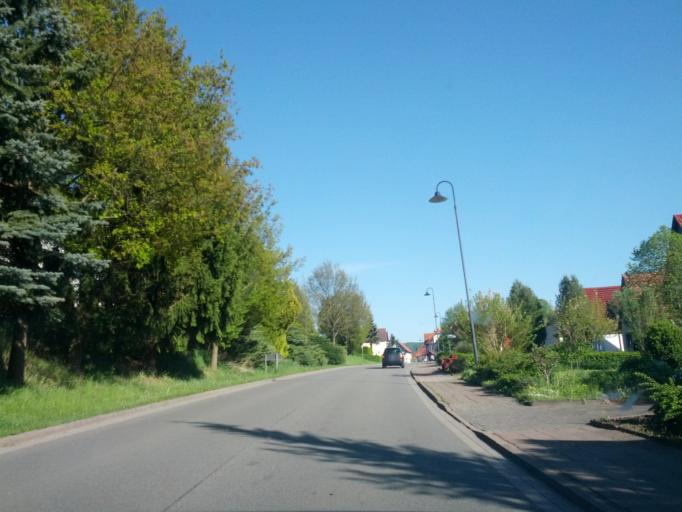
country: DE
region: Thuringia
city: Geismar
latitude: 51.2344
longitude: 10.1608
